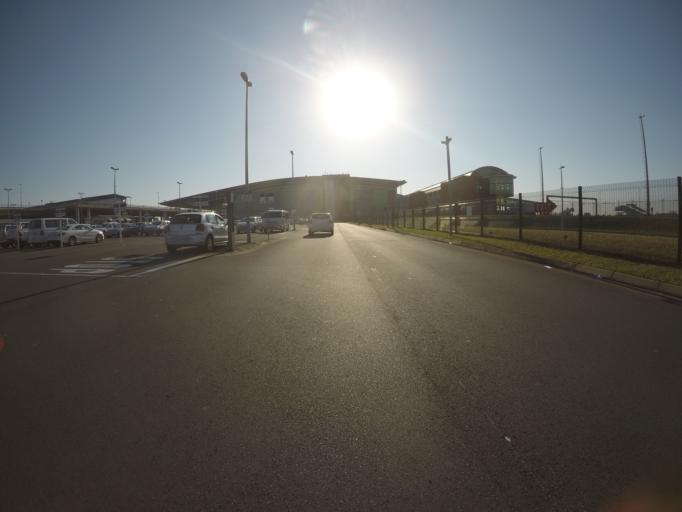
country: ZA
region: KwaZulu-Natal
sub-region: iLembe District Municipality
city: Ballitoville
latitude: -29.6210
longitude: 31.1034
